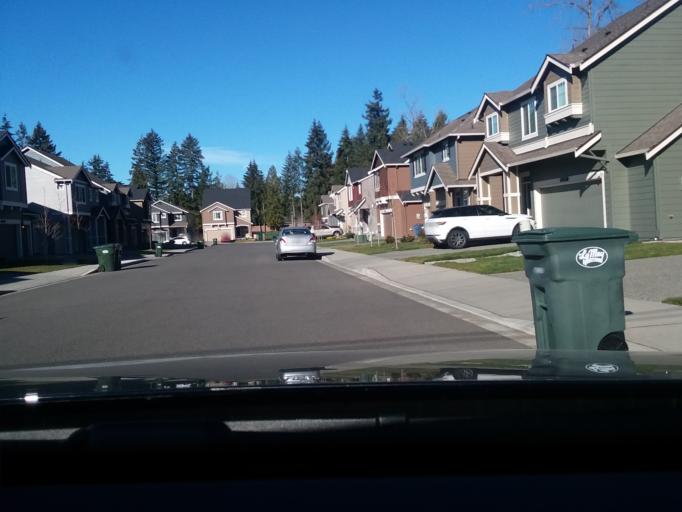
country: US
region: Washington
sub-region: Pierce County
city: Frederickson
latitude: 47.0980
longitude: -122.3203
